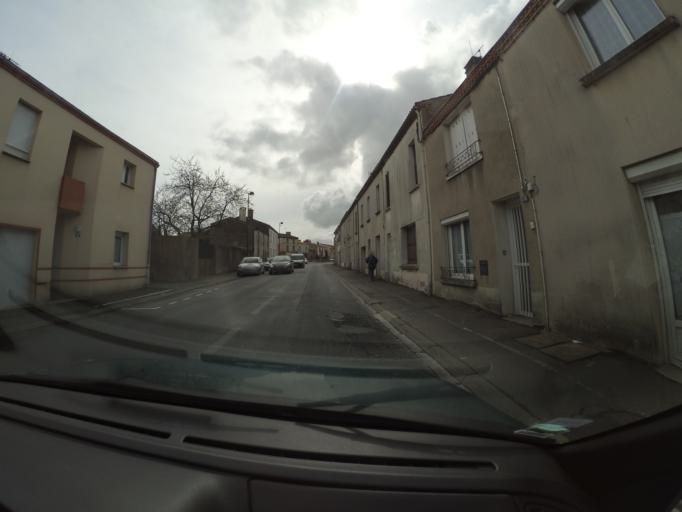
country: FR
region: Pays de la Loire
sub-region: Departement de Maine-et-Loire
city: Saint-Laurent-des-Autels
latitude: 47.2871
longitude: -1.1892
